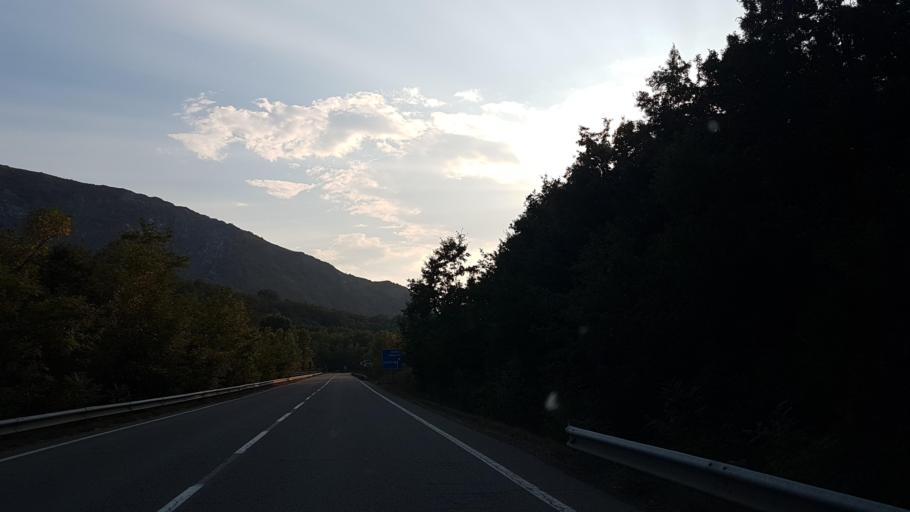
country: IT
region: Emilia-Romagna
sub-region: Provincia di Parma
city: Stazione Valmozzola
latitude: 44.5412
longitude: 9.8983
